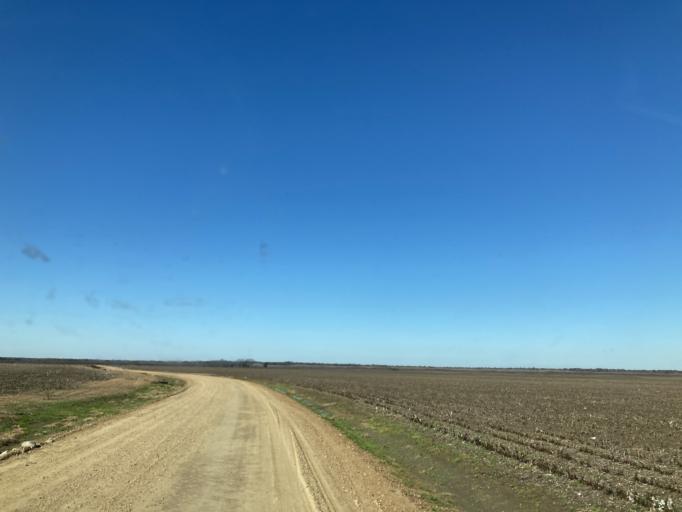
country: US
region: Mississippi
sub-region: Sharkey County
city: Rolling Fork
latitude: 32.8224
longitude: -90.7304
